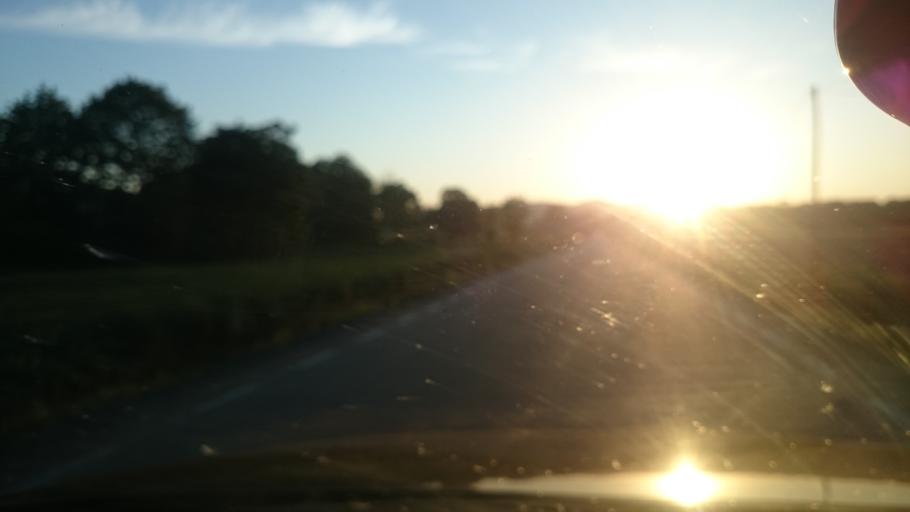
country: PL
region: Lower Silesian Voivodeship
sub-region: Powiat zabkowicki
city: Bardo
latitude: 50.5075
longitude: 16.7963
